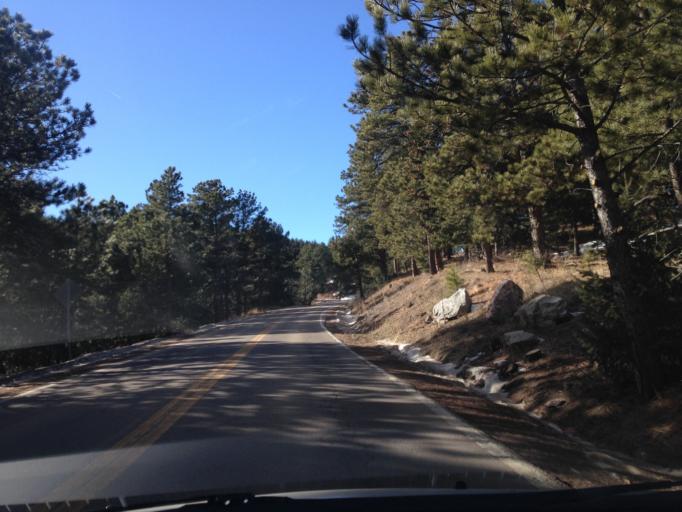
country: US
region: Colorado
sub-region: Boulder County
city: Boulder
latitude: 39.9969
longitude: -105.3094
